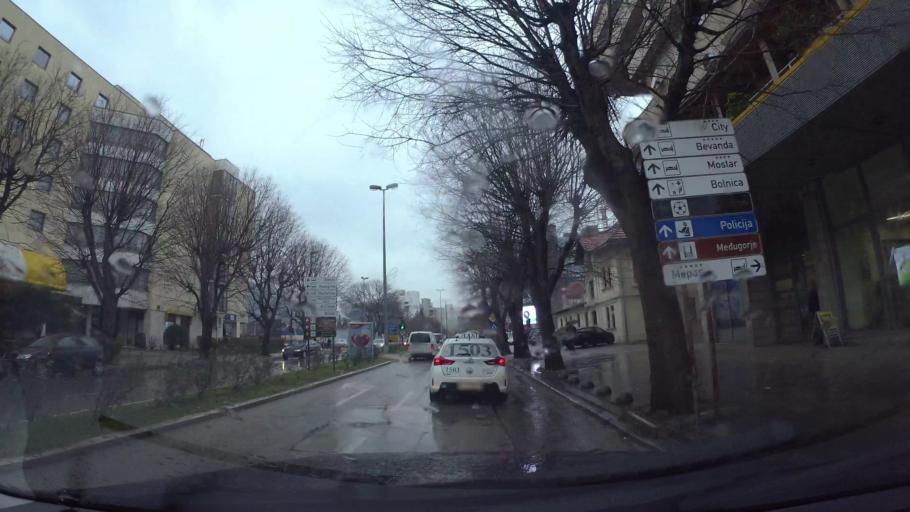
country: BA
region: Federation of Bosnia and Herzegovina
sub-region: Hercegovacko-Bosanski Kanton
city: Mostar
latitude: 43.3481
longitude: 17.8076
